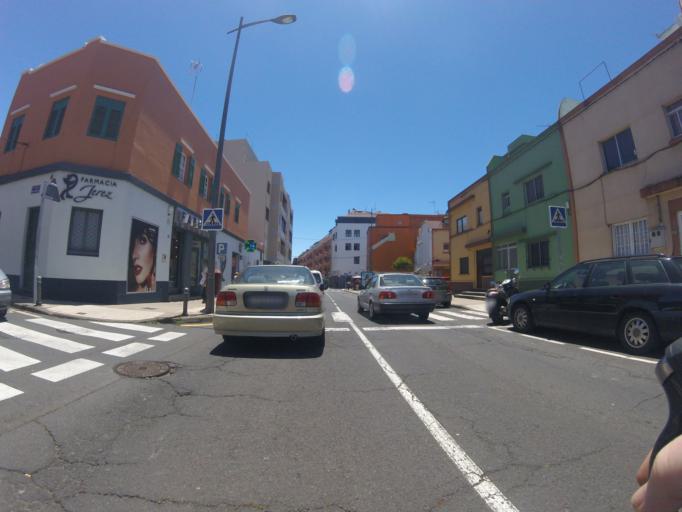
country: ES
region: Canary Islands
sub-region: Provincia de Santa Cruz de Tenerife
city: La Laguna
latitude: 28.4876
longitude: -16.3196
